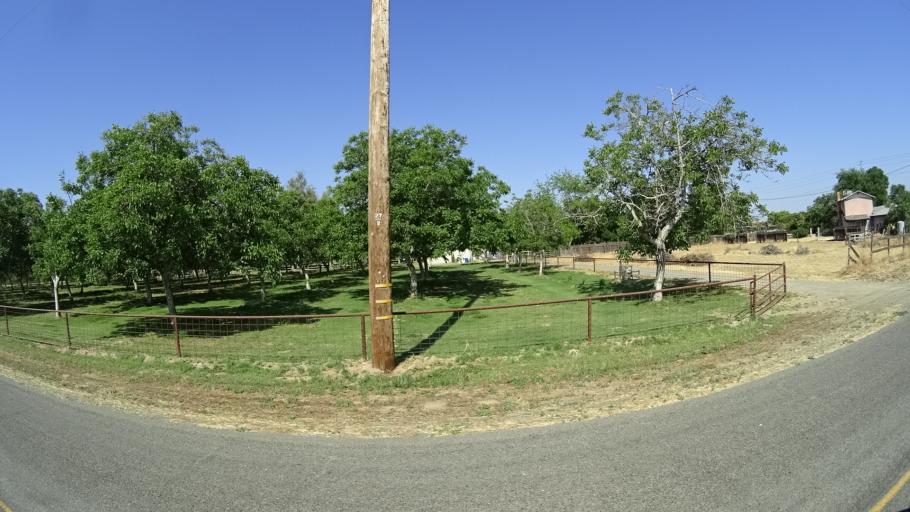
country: US
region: California
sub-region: Kings County
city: Hanford
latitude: 36.3416
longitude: -119.5831
